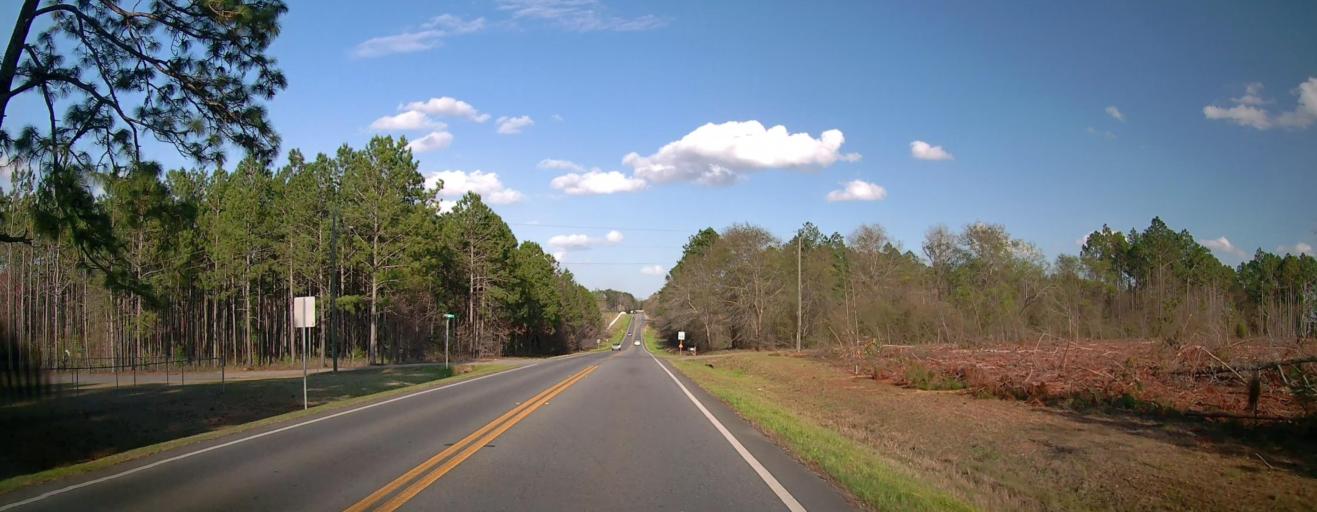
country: US
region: Georgia
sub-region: Toombs County
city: Vidalia
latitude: 32.2132
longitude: -82.4594
